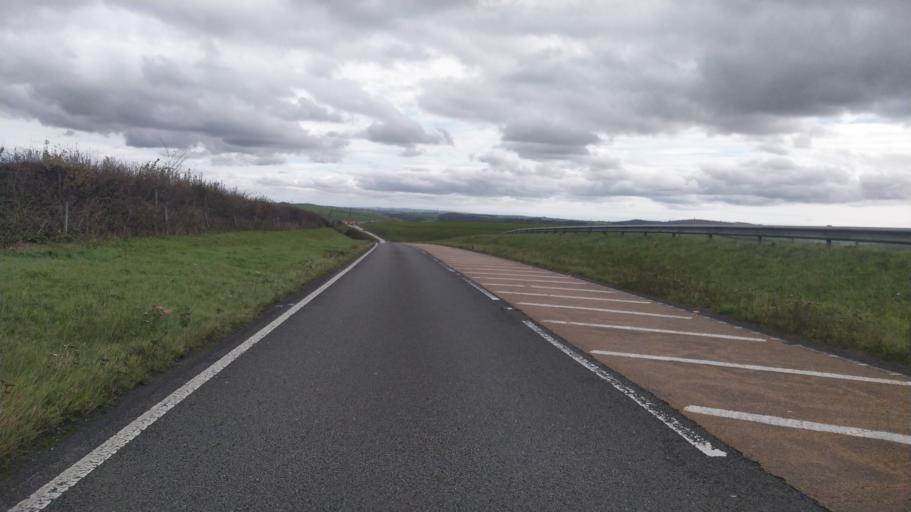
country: GB
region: England
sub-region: Dorset
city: Bridport
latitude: 50.7212
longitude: -2.6183
